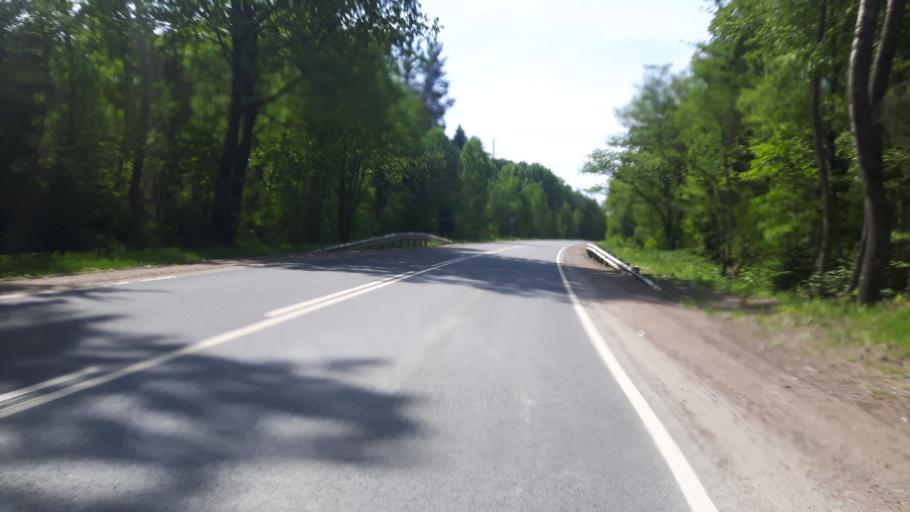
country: RU
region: Leningrad
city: Vistino
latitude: 59.6879
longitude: 28.4608
